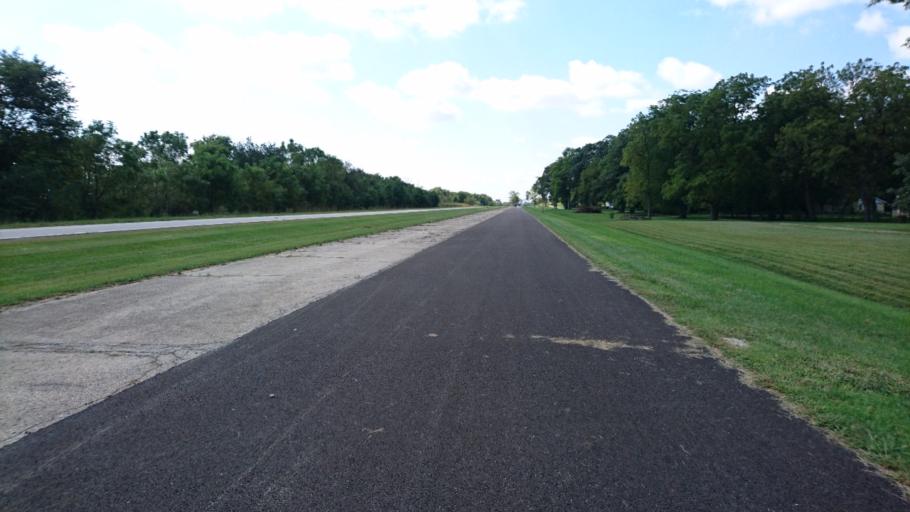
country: US
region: Illinois
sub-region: McLean County
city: Lexington
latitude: 40.5828
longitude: -88.8707
